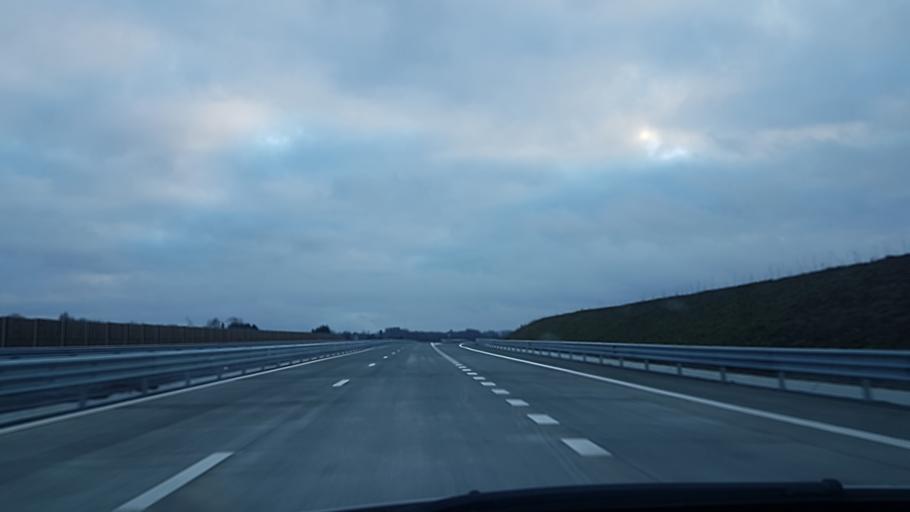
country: FR
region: Champagne-Ardenne
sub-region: Departement des Ardennes
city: Rocroi
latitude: 49.9662
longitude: 4.5360
